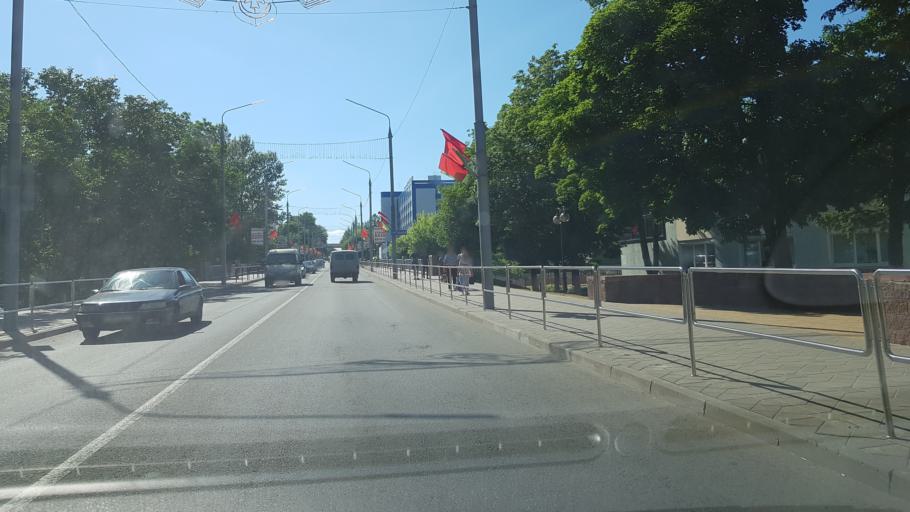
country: BY
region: Vitebsk
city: Orsha
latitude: 54.5127
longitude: 30.4218
